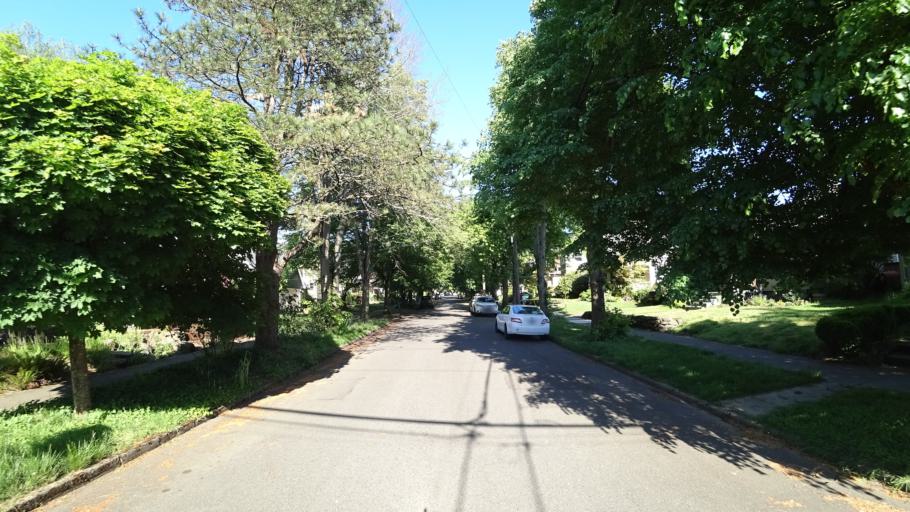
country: US
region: Oregon
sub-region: Multnomah County
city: Portland
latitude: 45.5279
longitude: -122.6328
